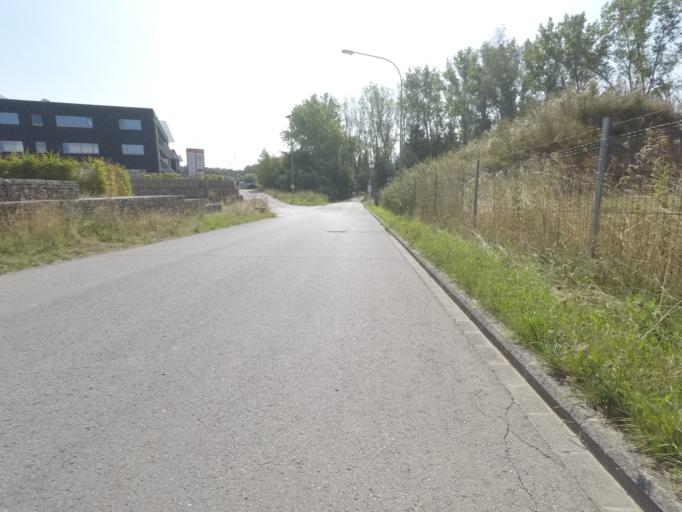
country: LU
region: Luxembourg
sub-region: Canton de Luxembourg
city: Olm
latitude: 49.6618
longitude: 6.0139
